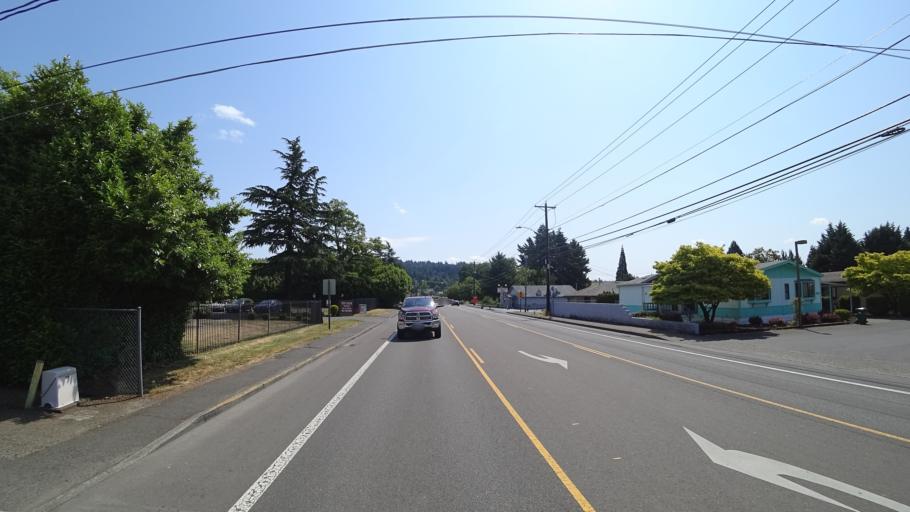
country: US
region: Oregon
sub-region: Multnomah County
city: Lents
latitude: 45.4471
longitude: -122.5826
